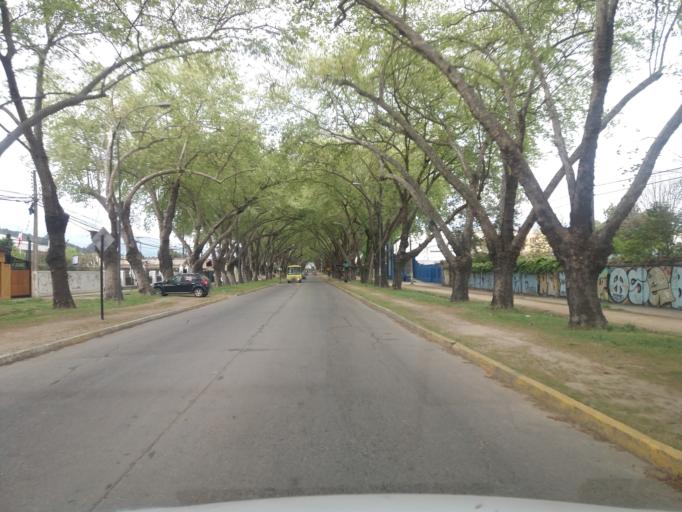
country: CL
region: Valparaiso
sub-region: Provincia de Marga Marga
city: Limache
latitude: -32.9877
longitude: -71.2703
